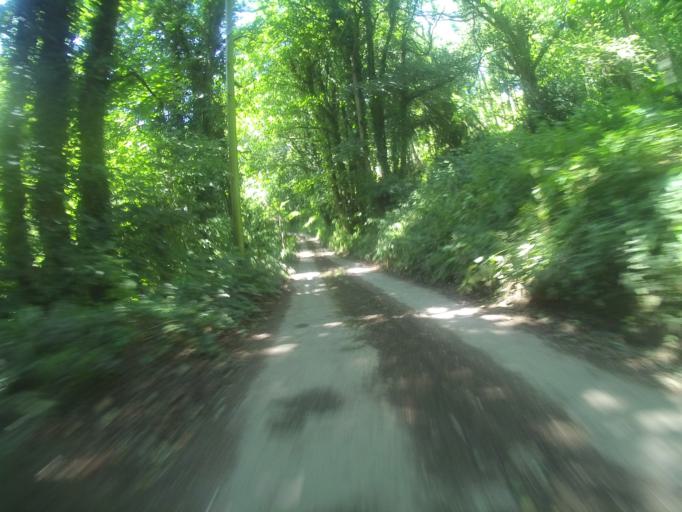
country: GB
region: England
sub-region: Devon
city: Dartmouth
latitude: 50.3579
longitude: -3.6092
